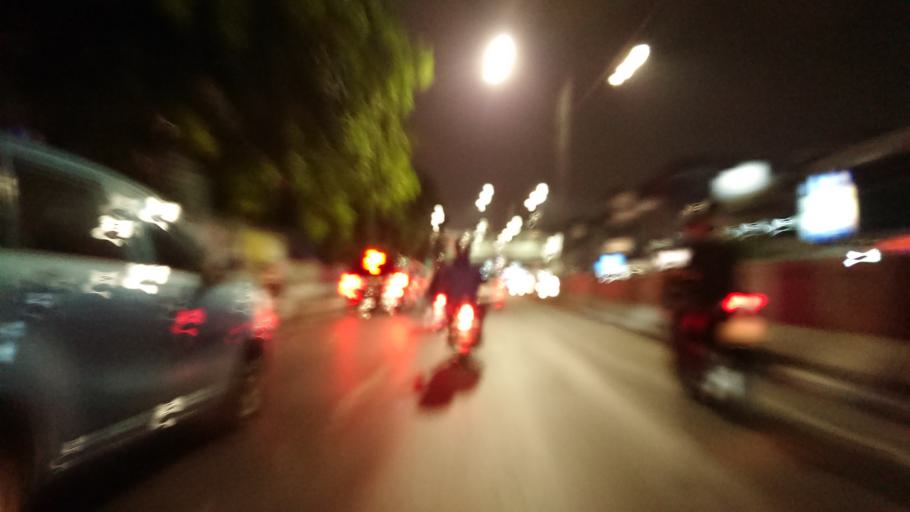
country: ID
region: Jakarta Raya
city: Jakarta
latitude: -6.1912
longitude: 106.8150
